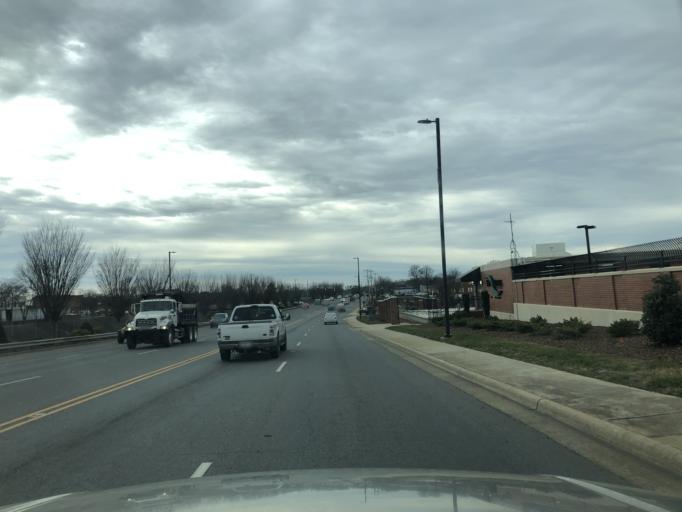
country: US
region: North Carolina
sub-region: Gaston County
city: Gastonia
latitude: 35.2654
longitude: -81.1833
